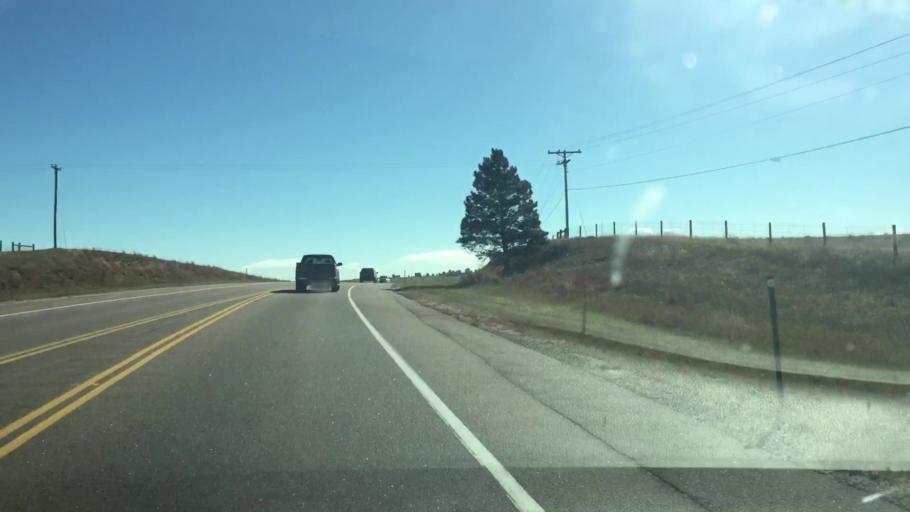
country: US
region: Colorado
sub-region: Elbert County
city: Elizabeth
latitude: 39.3613
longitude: -104.5474
